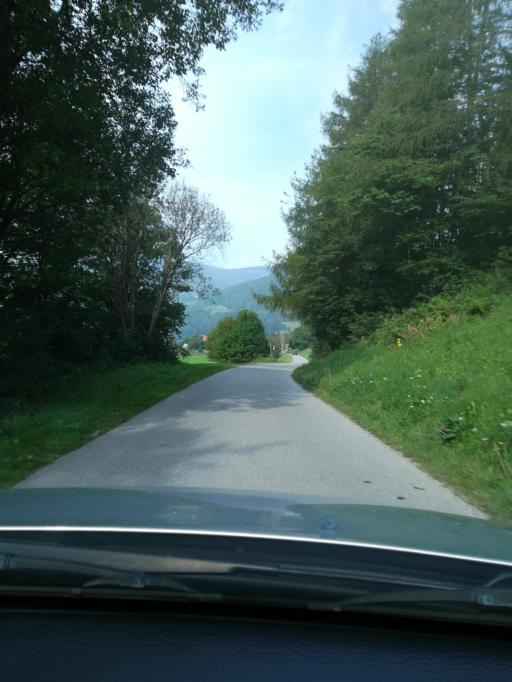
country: AT
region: Styria
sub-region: Politischer Bezirk Murtal
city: Sankt Georgen ob Judenburg
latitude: 47.2158
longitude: 14.4755
